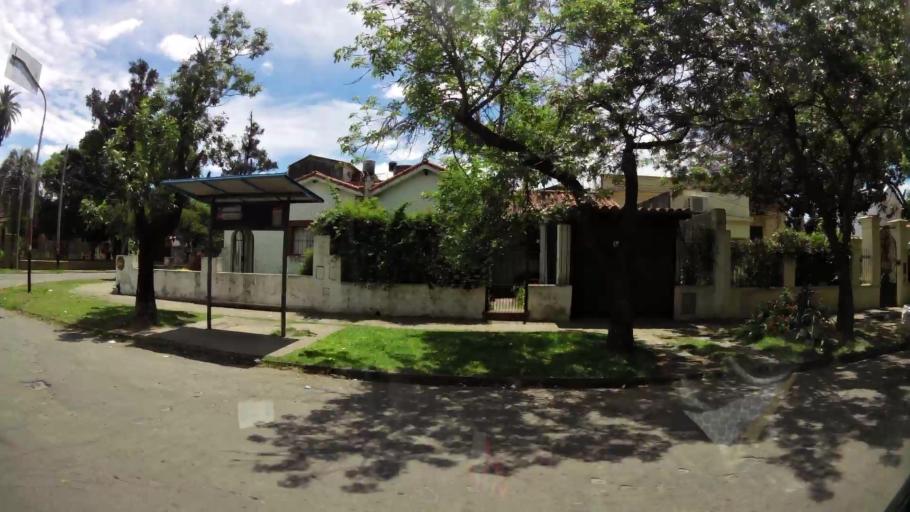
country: AR
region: Santa Fe
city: Gobernador Galvez
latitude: -33.0023
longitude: -60.6263
